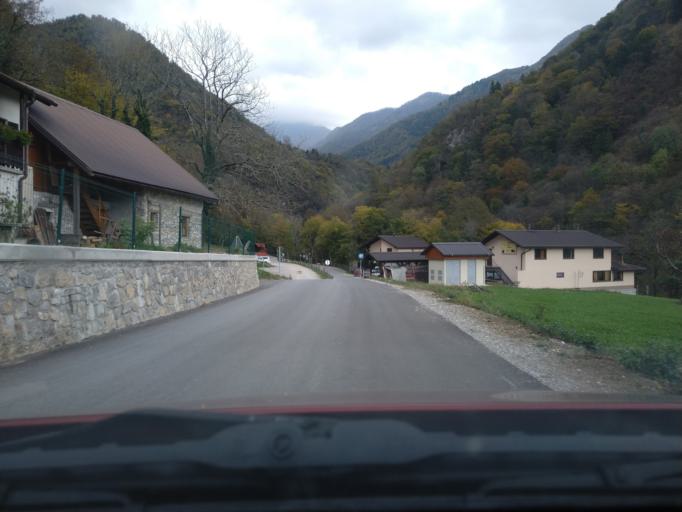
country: SI
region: Tolmin
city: Tolmin
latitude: 46.1971
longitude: 13.7384
